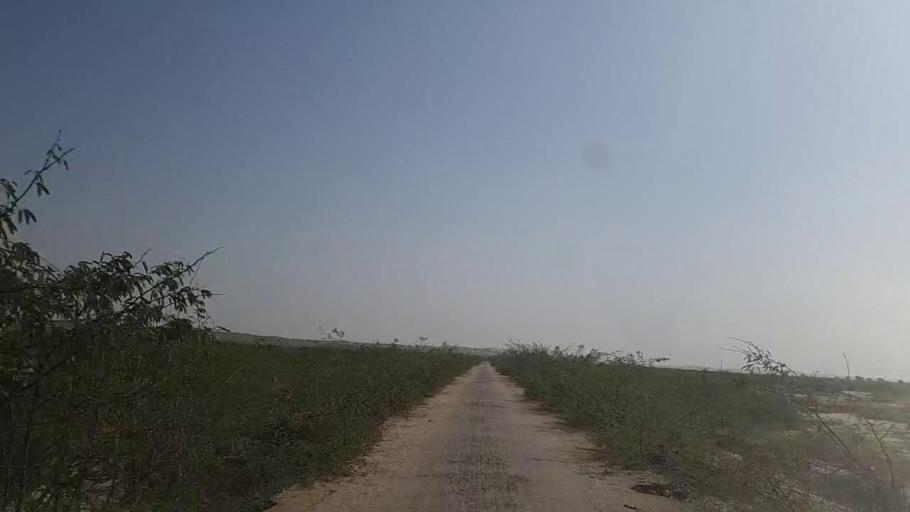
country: PK
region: Sindh
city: Naukot
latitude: 24.5919
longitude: 69.2924
